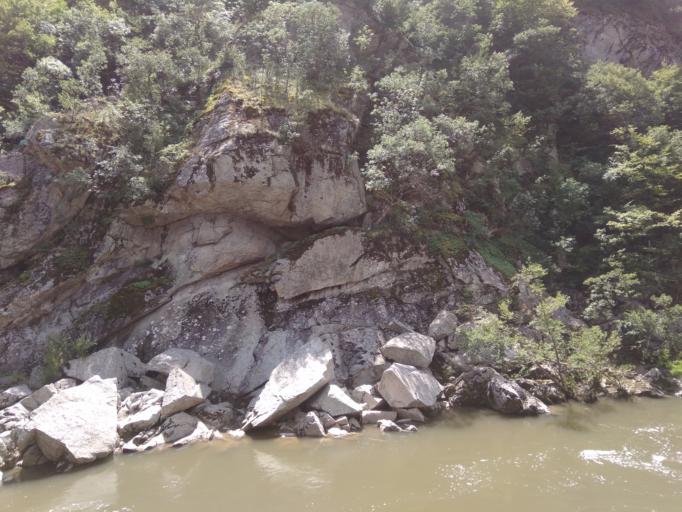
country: BG
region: Kurdzhali
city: Ardino
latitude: 41.6207
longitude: 25.1139
